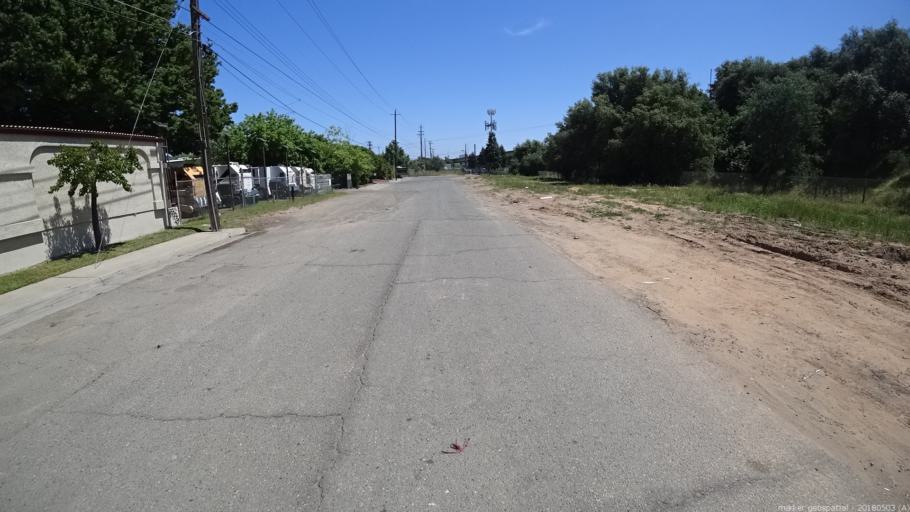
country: US
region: California
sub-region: Sacramento County
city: Arden-Arcade
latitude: 38.6381
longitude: -121.4082
